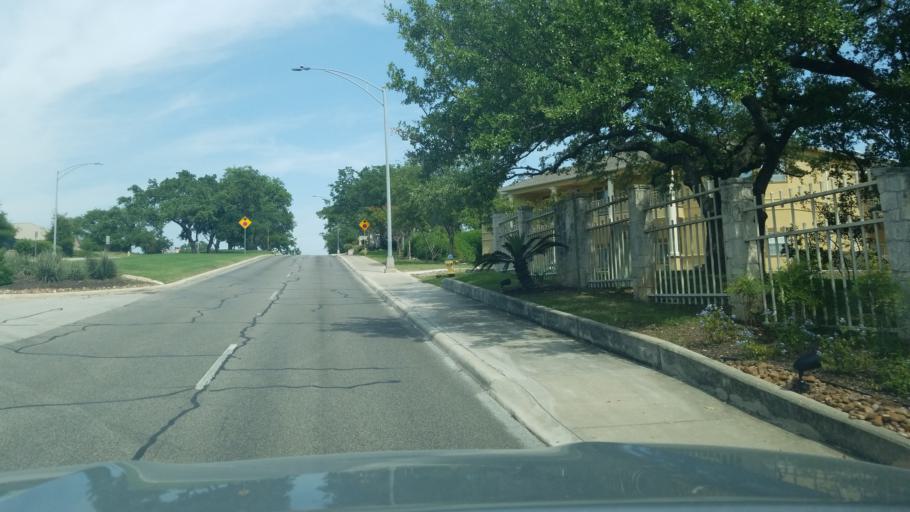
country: US
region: Texas
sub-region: Bexar County
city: Hollywood Park
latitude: 29.6261
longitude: -98.4905
